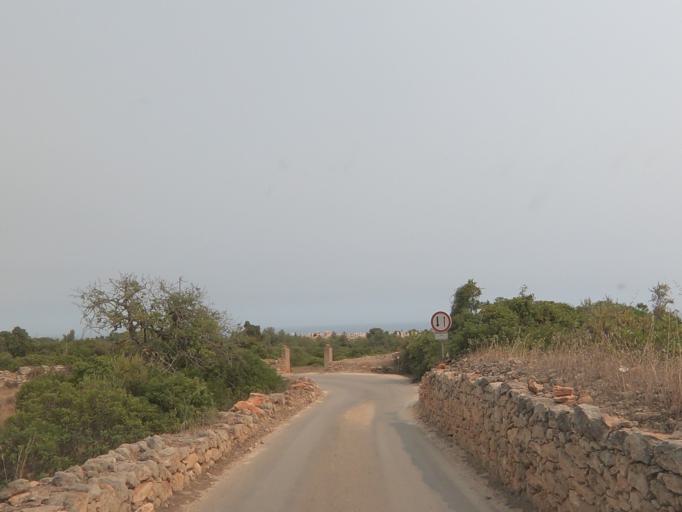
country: PT
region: Faro
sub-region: Lagoa
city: Carvoeiro
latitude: 37.0955
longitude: -8.4066
